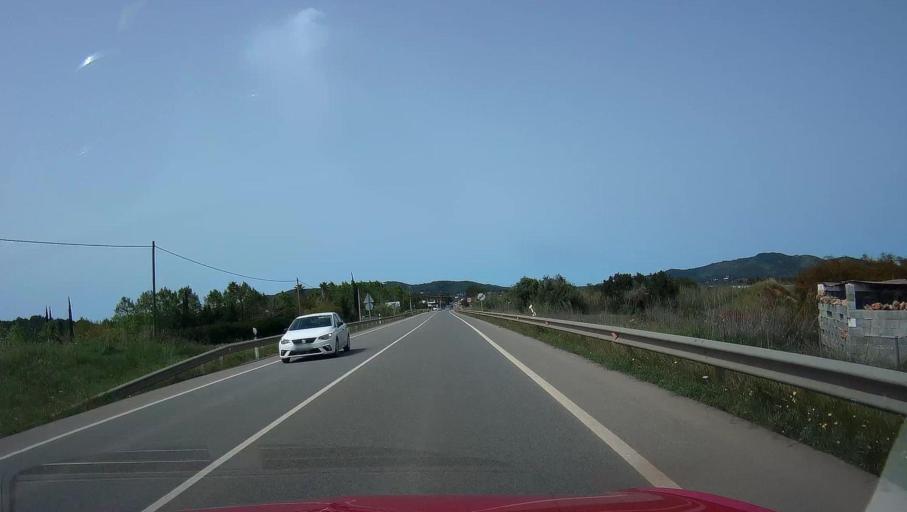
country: ES
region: Balearic Islands
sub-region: Illes Balears
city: Santa Eularia des Riu
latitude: 39.0074
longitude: 1.4881
